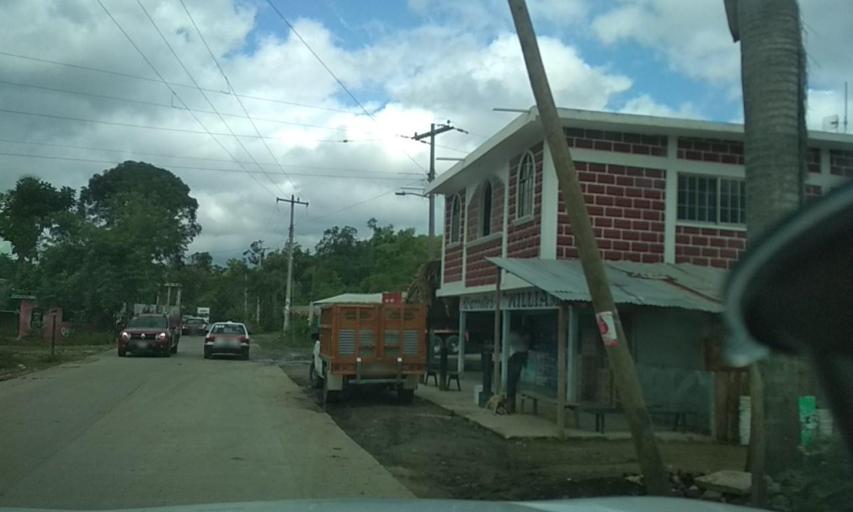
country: MX
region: Veracruz
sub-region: Papantla
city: Polutla
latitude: 20.5411
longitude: -97.2525
